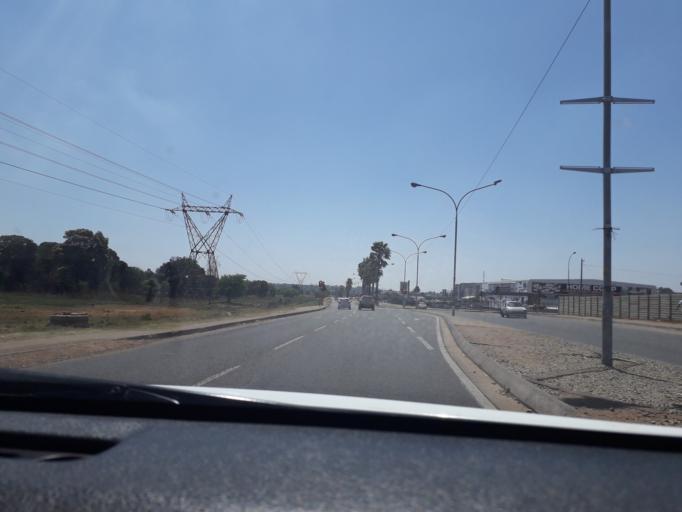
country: ZA
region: Gauteng
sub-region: City of Johannesburg Metropolitan Municipality
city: Modderfontein
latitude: -26.1090
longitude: 28.2224
